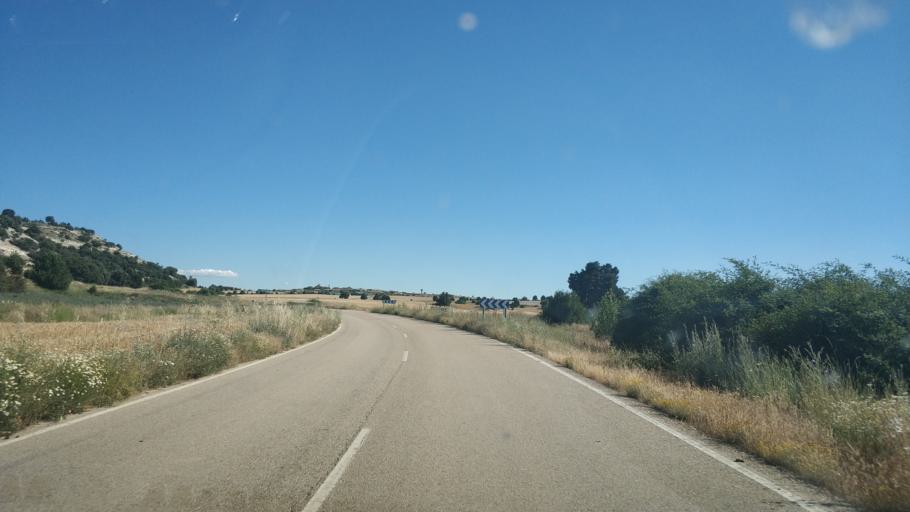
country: ES
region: Castille and Leon
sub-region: Provincia de Soria
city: San Esteban de Gormaz
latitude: 41.4782
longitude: -3.2159
